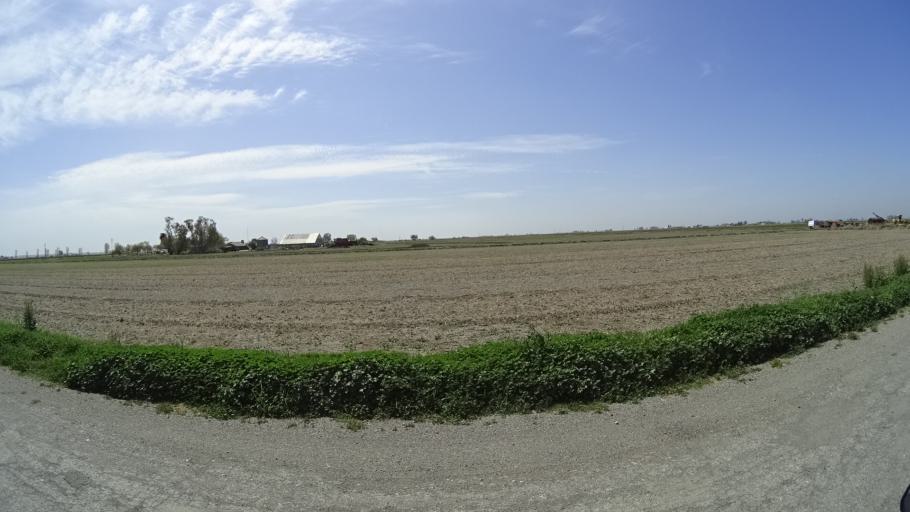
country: US
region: California
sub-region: Glenn County
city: Willows
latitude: 39.5731
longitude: -122.0682
